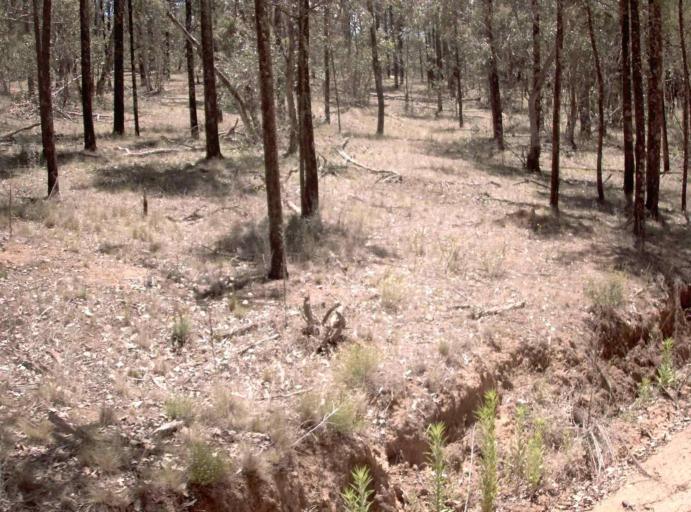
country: AU
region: New South Wales
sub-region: Snowy River
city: Jindabyne
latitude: -36.8978
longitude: 148.4185
